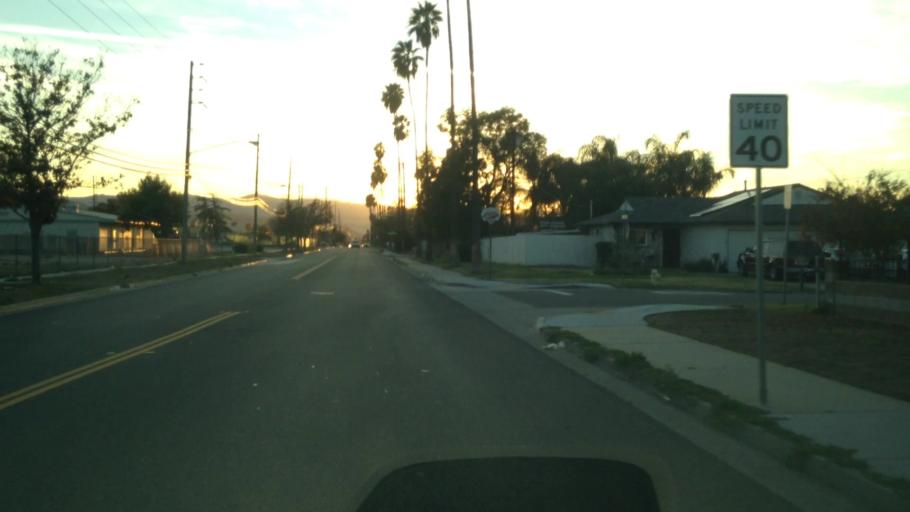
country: US
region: California
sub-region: Riverside County
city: Riverside
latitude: 33.9180
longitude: -117.4346
